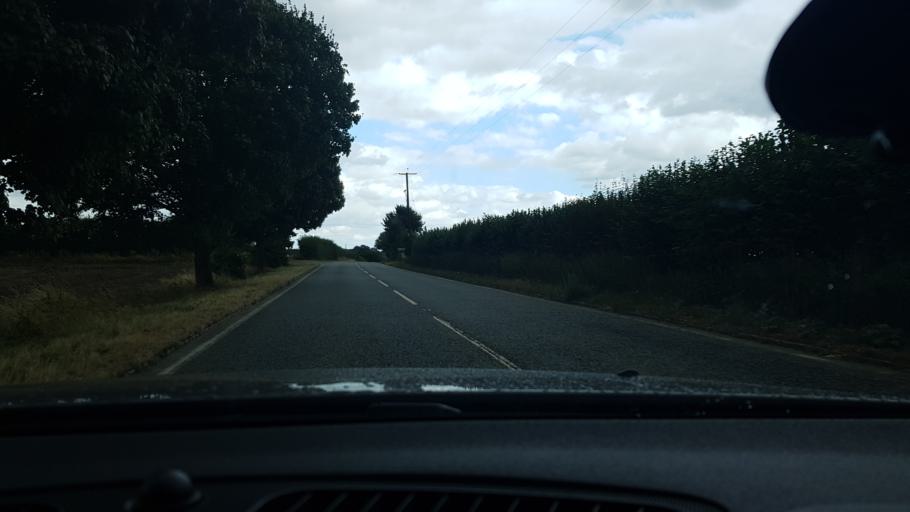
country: GB
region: England
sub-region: West Berkshire
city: Wickham
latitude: 51.4523
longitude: -1.4616
